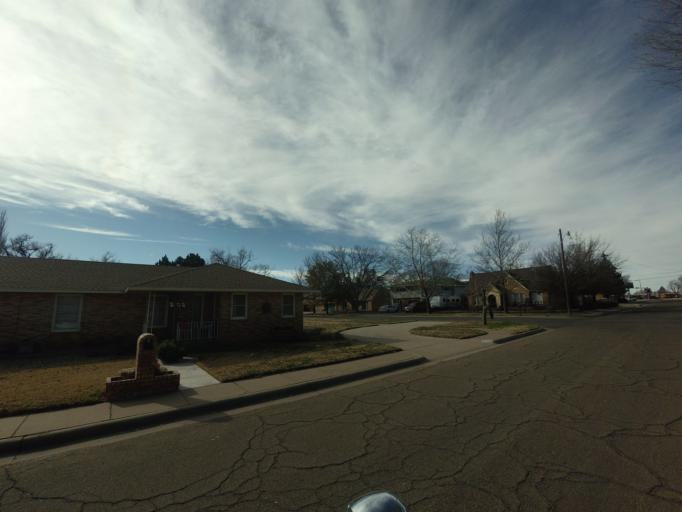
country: US
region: New Mexico
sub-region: Curry County
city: Clovis
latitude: 34.4139
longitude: -103.2025
